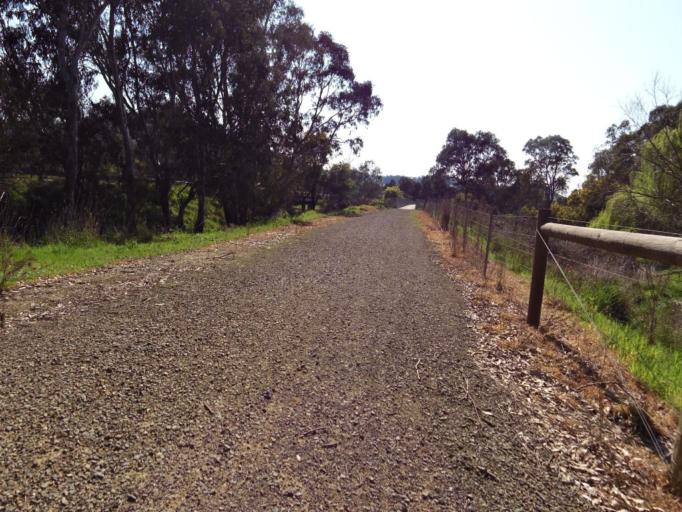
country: AU
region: Victoria
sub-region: Murrindindi
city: Alexandra
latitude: -37.1655
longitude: 145.5434
